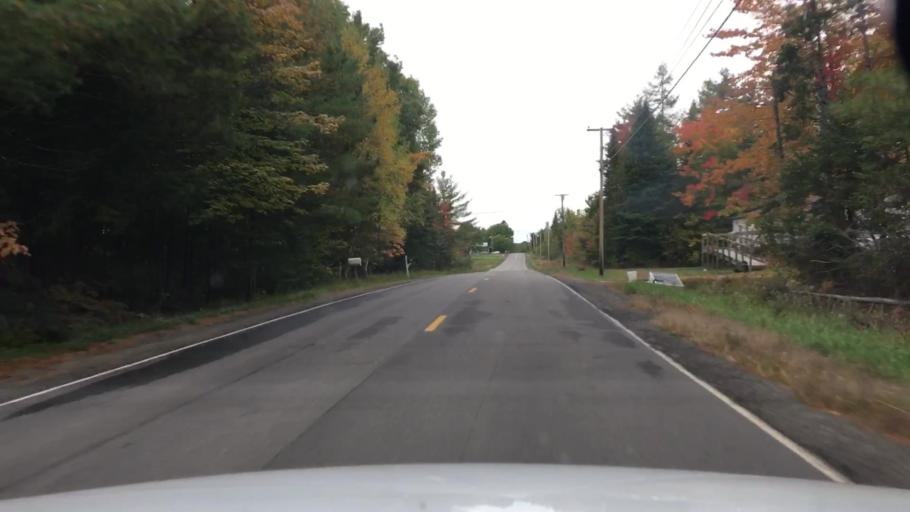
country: US
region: Maine
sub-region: Penobscot County
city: Hudson
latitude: 44.9883
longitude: -68.7621
